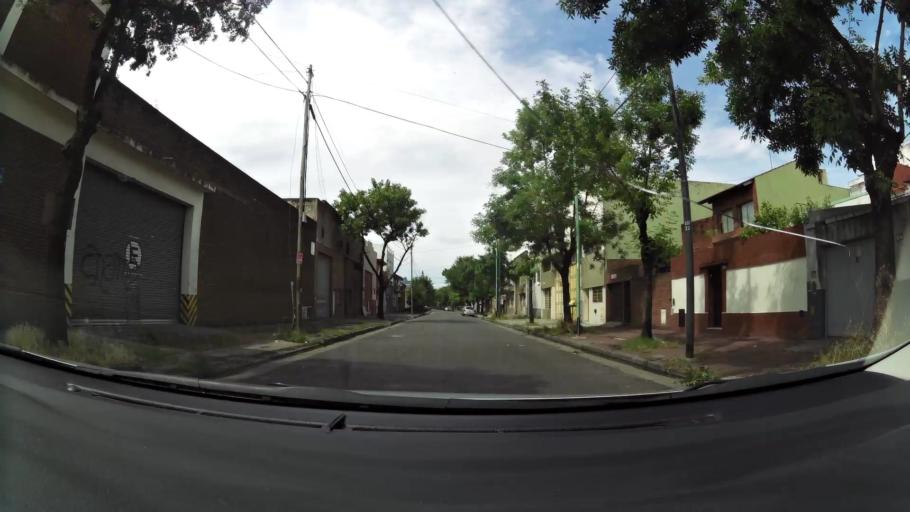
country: AR
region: Buenos Aires F.D.
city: Villa Lugano
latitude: -34.6611
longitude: -58.4278
